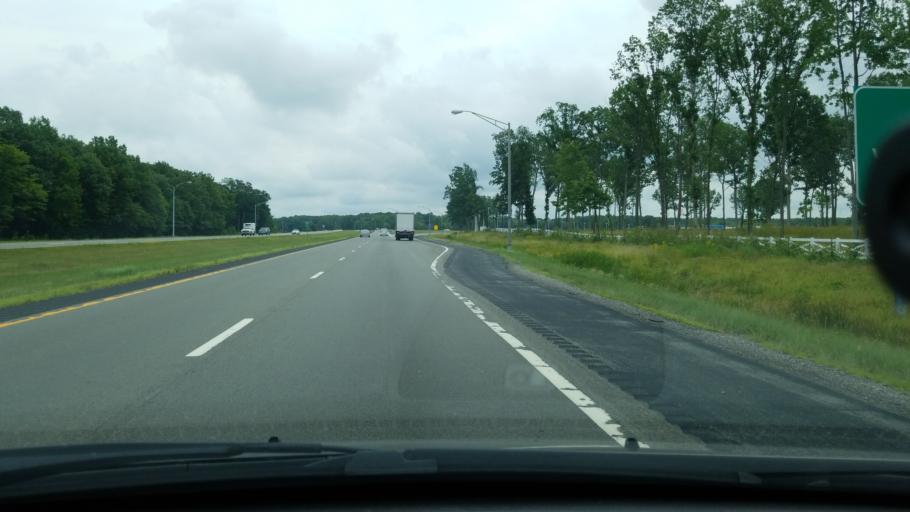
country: US
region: Ohio
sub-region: Lorain County
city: Vermilion
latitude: 41.3977
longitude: -82.3724
